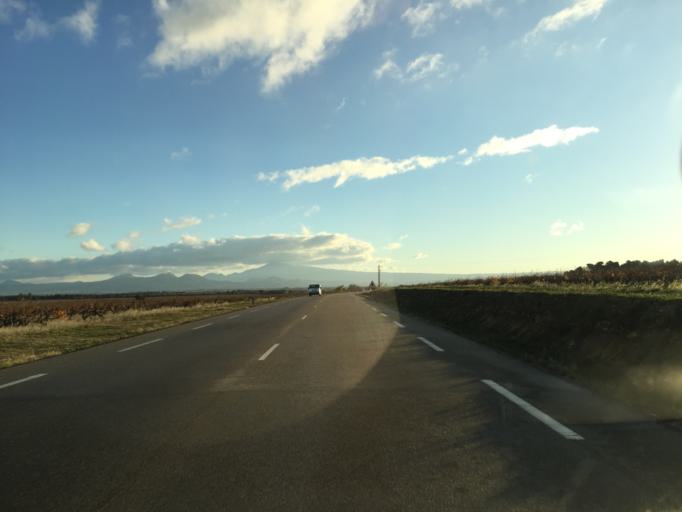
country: FR
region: Provence-Alpes-Cote d'Azur
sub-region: Departement du Vaucluse
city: Courthezon
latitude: 44.0965
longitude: 4.8435
